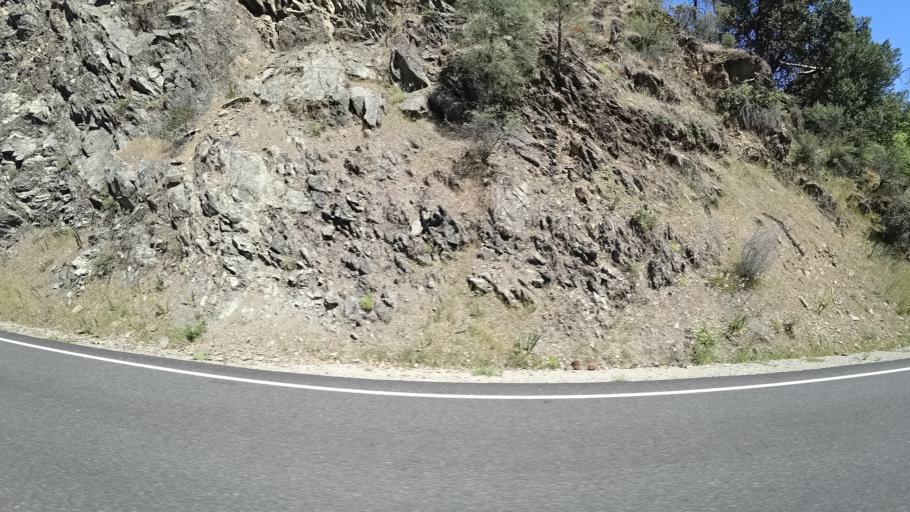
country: US
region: California
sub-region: Trinity County
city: Weaverville
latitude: 40.7435
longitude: -123.0651
